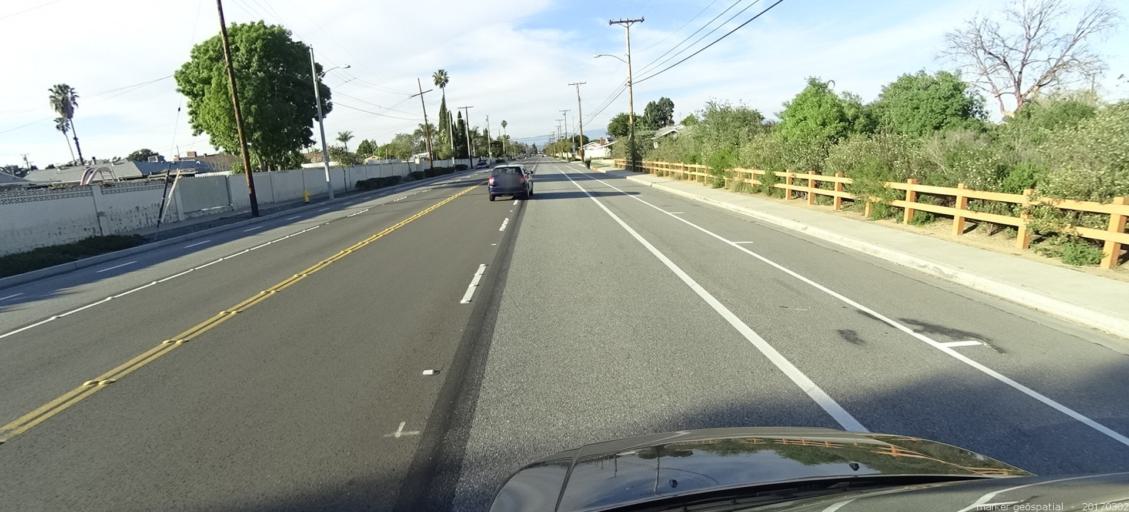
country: US
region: California
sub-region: Orange County
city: Anaheim
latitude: 33.8283
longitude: -117.8717
